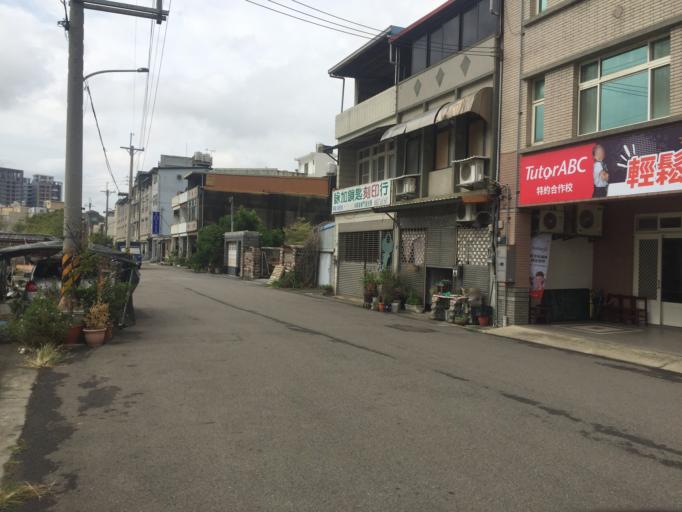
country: TW
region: Taiwan
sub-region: Hsinchu
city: Hsinchu
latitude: 24.6984
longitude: 120.8909
